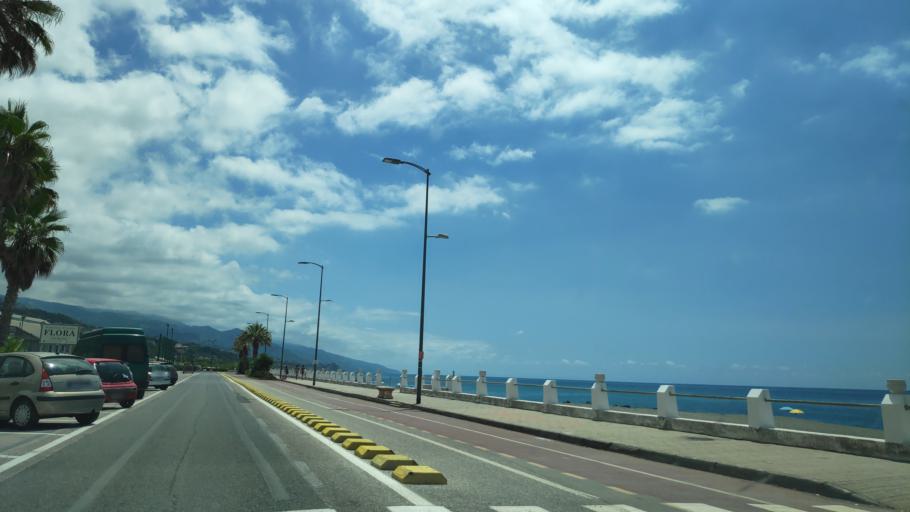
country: IT
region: Calabria
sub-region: Provincia di Cosenza
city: Paola
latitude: 39.3557
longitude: 16.0332
